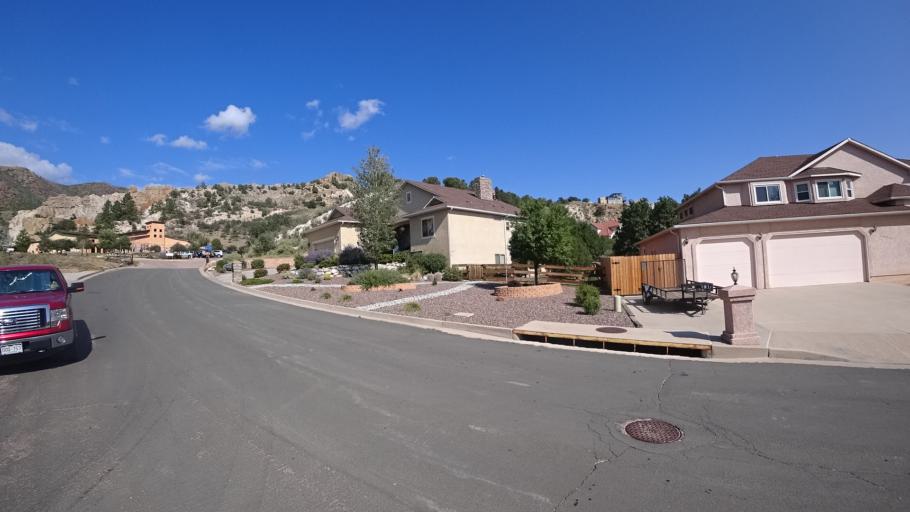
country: US
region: Colorado
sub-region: El Paso County
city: Manitou Springs
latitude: 38.9051
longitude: -104.8769
